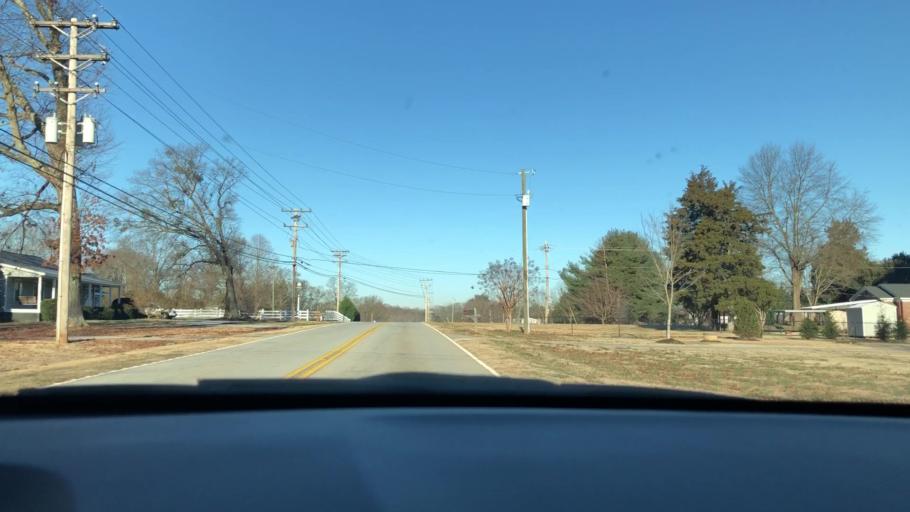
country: US
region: South Carolina
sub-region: Greenville County
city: Five Forks
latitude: 34.8210
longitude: -82.2104
